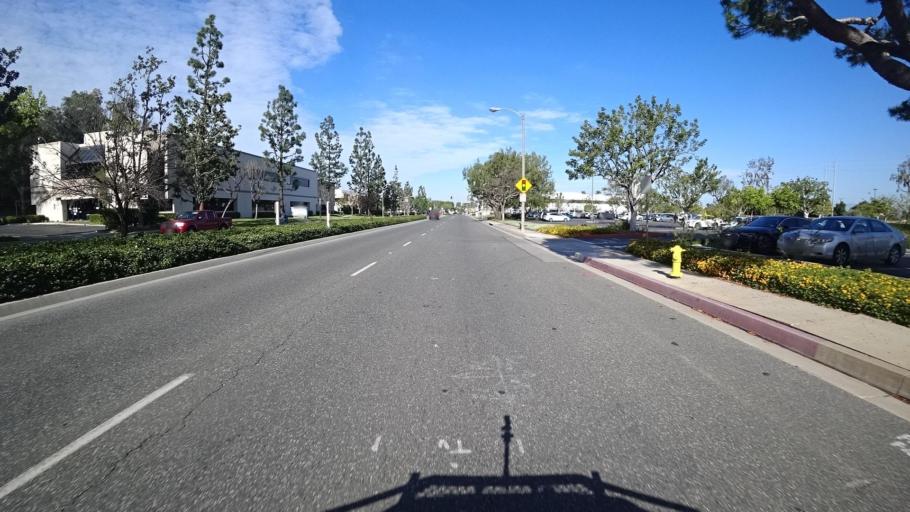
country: US
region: California
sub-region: Los Angeles County
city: Avocado Heights
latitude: 34.0289
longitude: -118.0222
